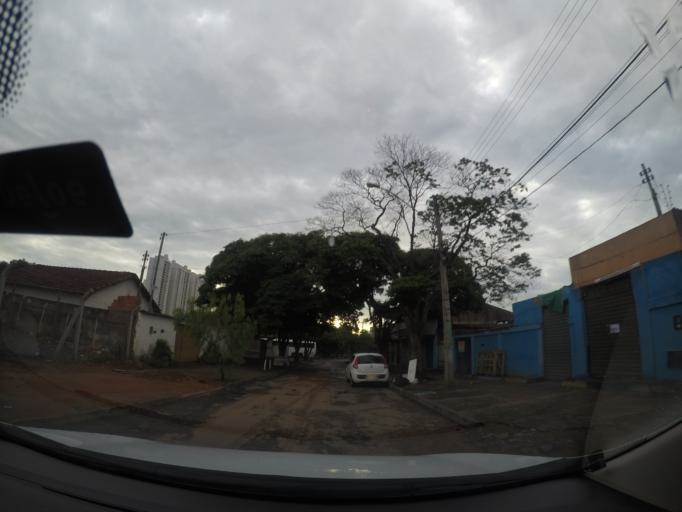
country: BR
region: Goias
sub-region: Goiania
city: Goiania
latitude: -16.6570
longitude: -49.2571
